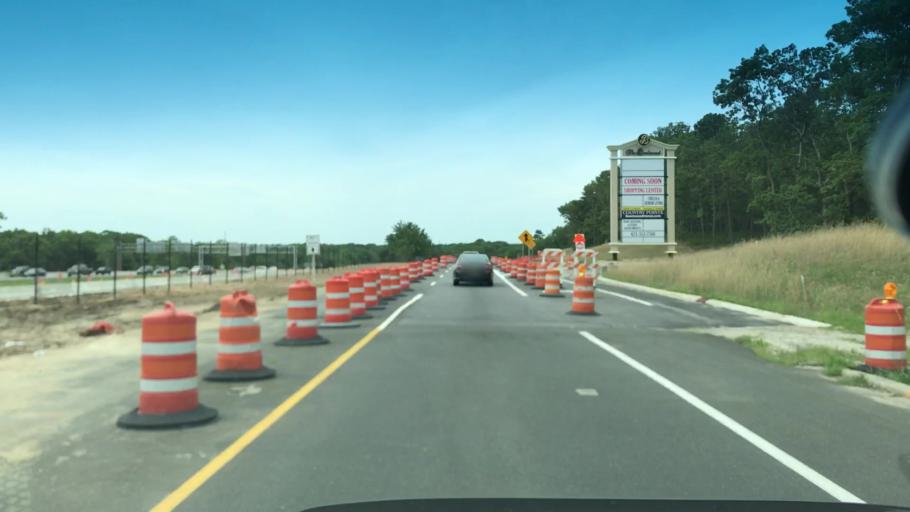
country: US
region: New York
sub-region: Suffolk County
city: Yaphank
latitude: 40.8408
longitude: -72.8977
